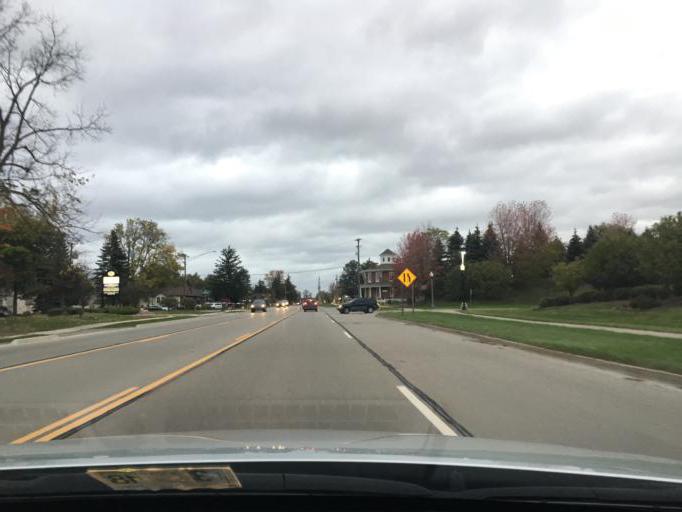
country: US
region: Michigan
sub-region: Macomb County
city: Shelby
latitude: 42.7158
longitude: -83.0354
